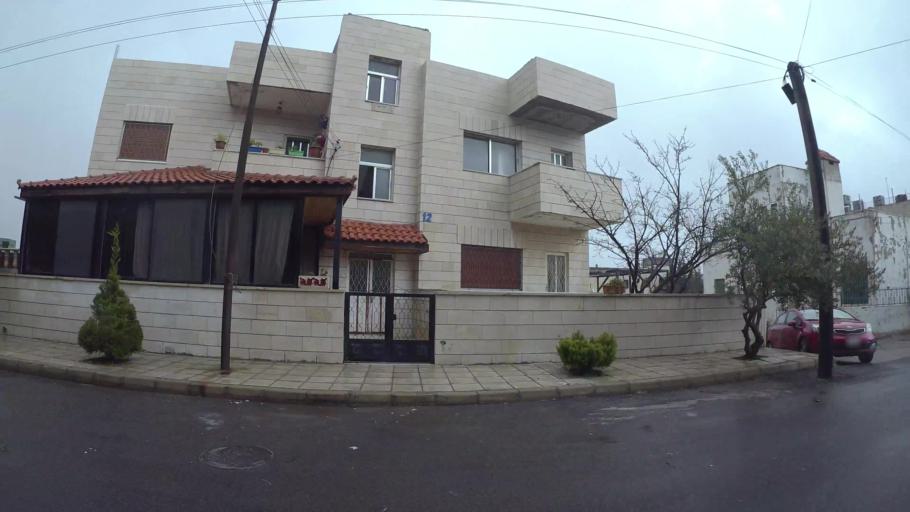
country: JO
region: Amman
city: Al Jubayhah
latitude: 32.0229
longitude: 35.8333
